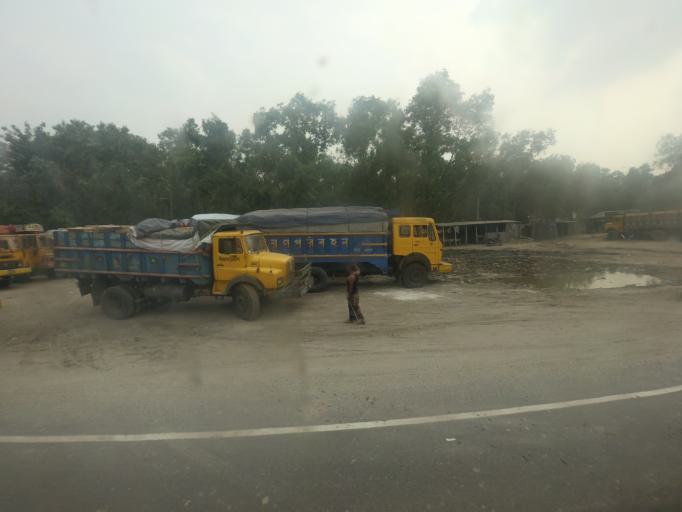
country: BD
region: Rajshahi
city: Sirajganj
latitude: 24.3893
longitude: 89.8194
